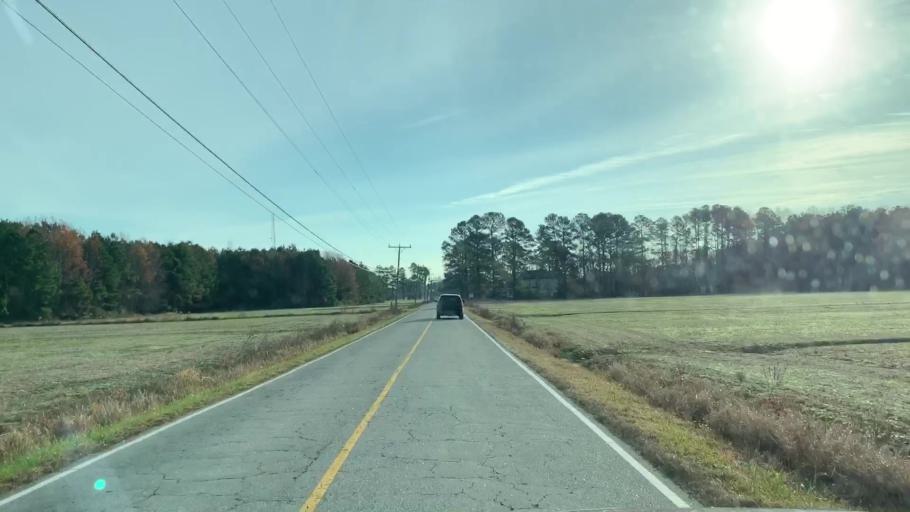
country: US
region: Virginia
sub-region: City of Virginia Beach
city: Virginia Beach
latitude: 36.6934
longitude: -76.0216
